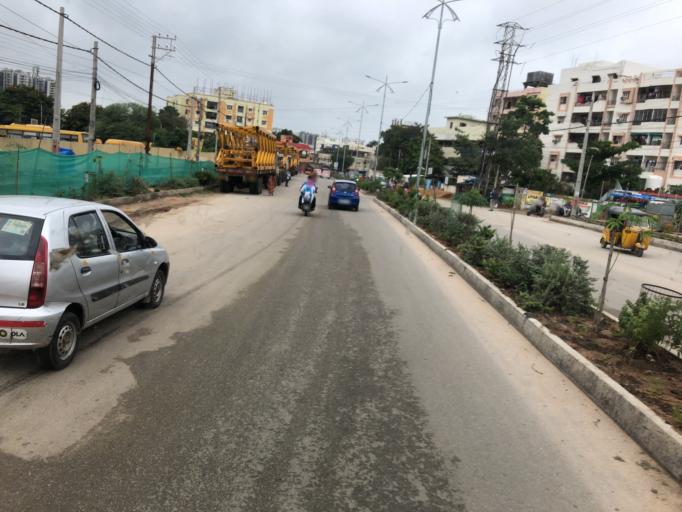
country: IN
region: Telangana
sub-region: Medak
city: Serilingampalle
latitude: 17.4646
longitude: 78.3450
